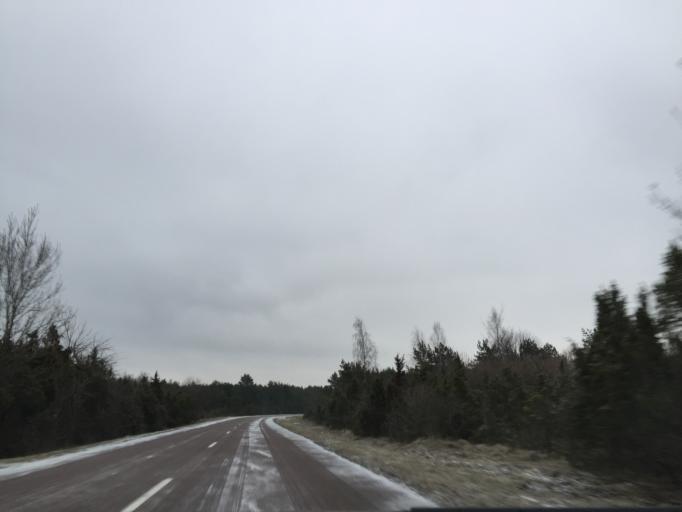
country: EE
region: Saare
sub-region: Orissaare vald
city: Orissaare
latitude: 58.6009
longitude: 23.1217
